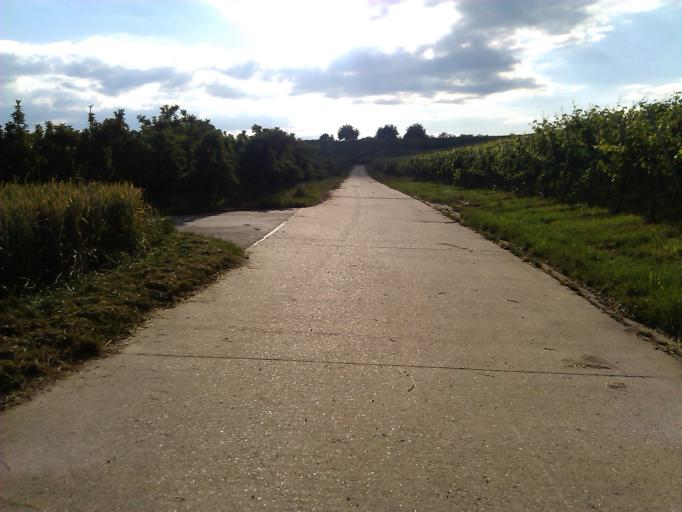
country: DE
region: Baden-Wuerttemberg
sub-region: Regierungsbezirk Stuttgart
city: Kirchheim am Neckar
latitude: 49.0527
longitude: 9.1593
